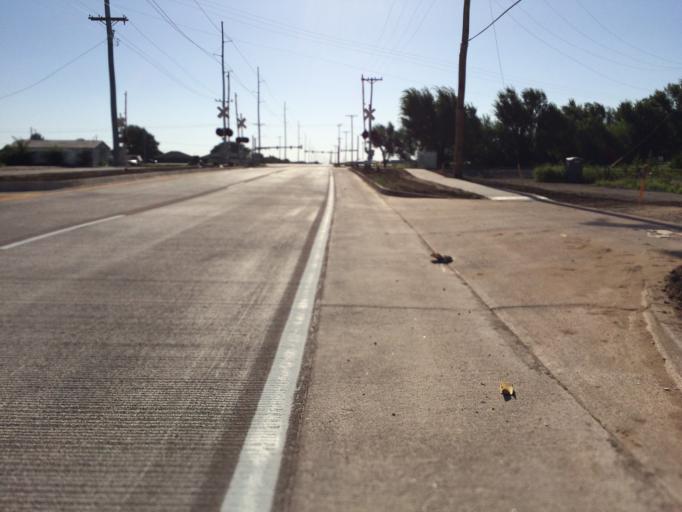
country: US
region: Oklahoma
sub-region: Cleveland County
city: Noble
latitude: 35.1751
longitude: -97.4154
